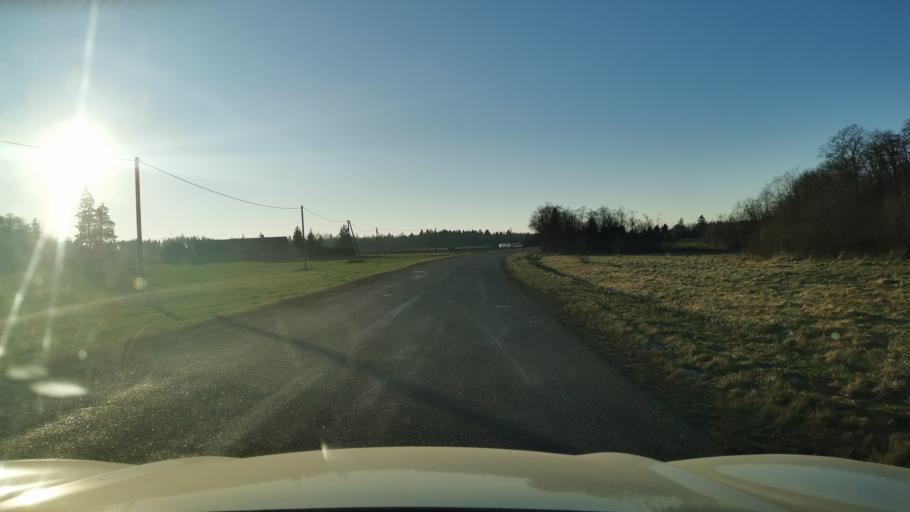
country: EE
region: Ida-Virumaa
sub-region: Kivioli linn
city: Kivioli
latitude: 59.3068
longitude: 26.9986
